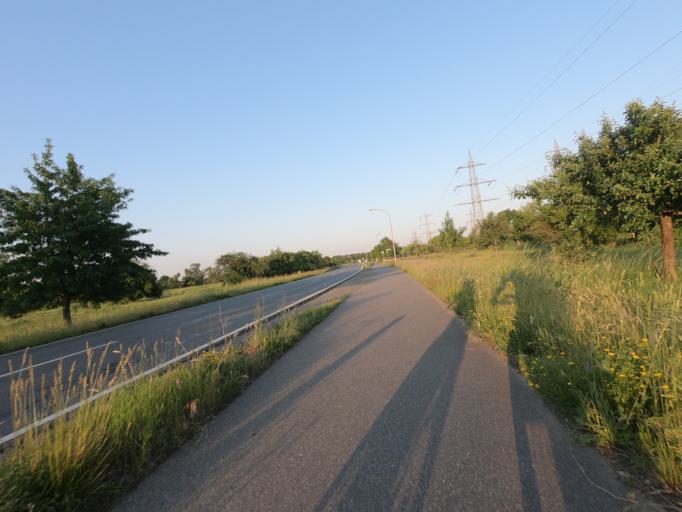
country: DE
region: Hesse
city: Morfelden-Walldorf
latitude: 49.9914
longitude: 8.5664
